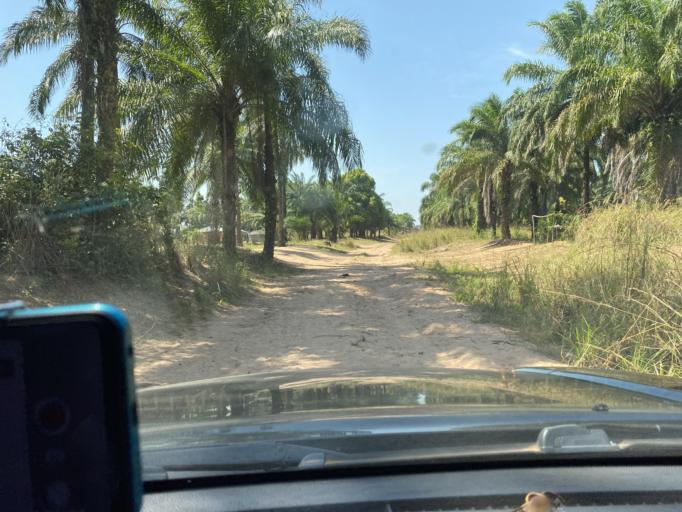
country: CD
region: Kasai-Oriental
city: Kabinda
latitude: -5.8747
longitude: 24.8821
